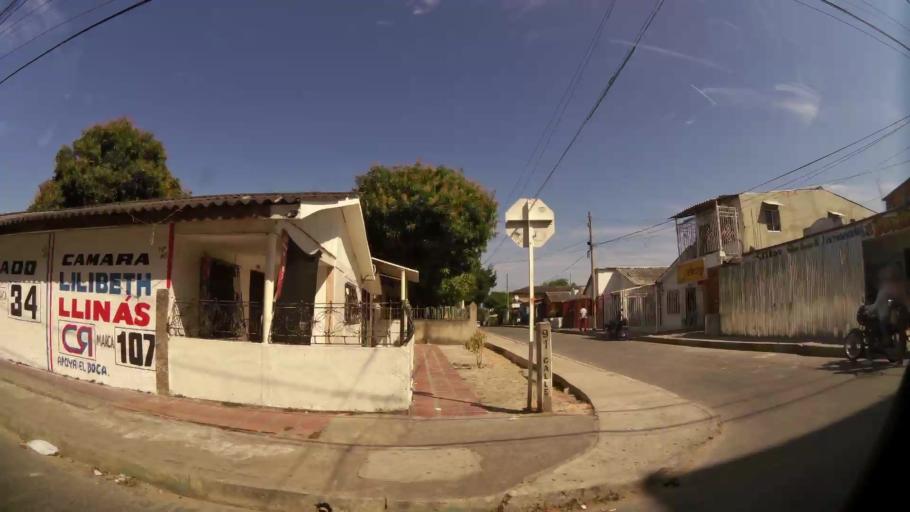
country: CO
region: Atlantico
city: Barranquilla
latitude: 10.9359
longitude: -74.8249
